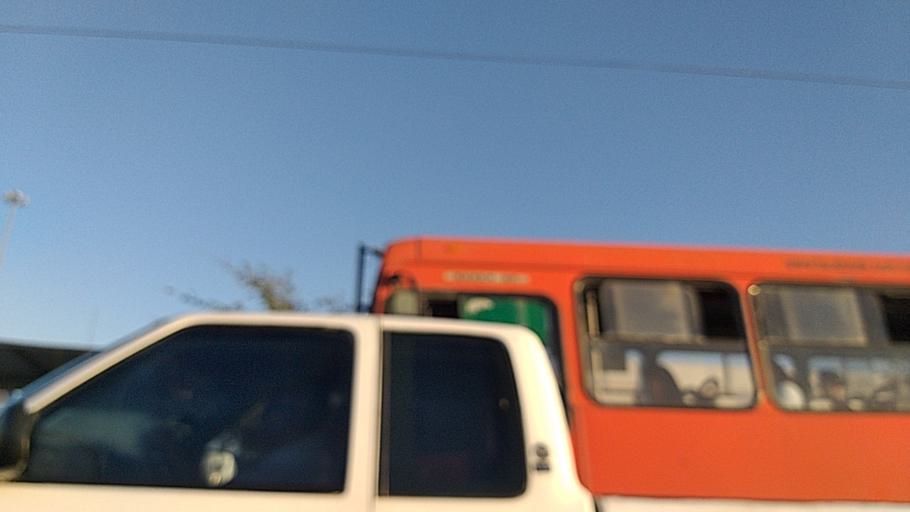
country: MX
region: Nuevo Leon
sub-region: Garcia
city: Mitras Poniente
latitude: 25.7648
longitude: -100.4116
